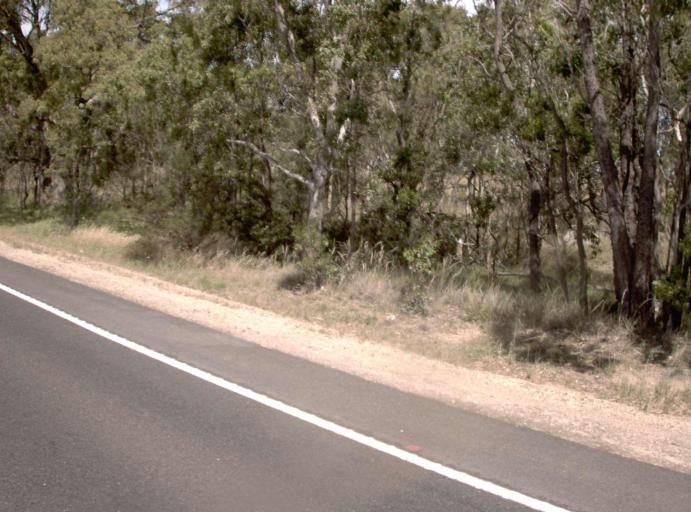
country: AU
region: Victoria
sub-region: East Gippsland
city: Bairnsdale
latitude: -37.8774
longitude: 147.4388
